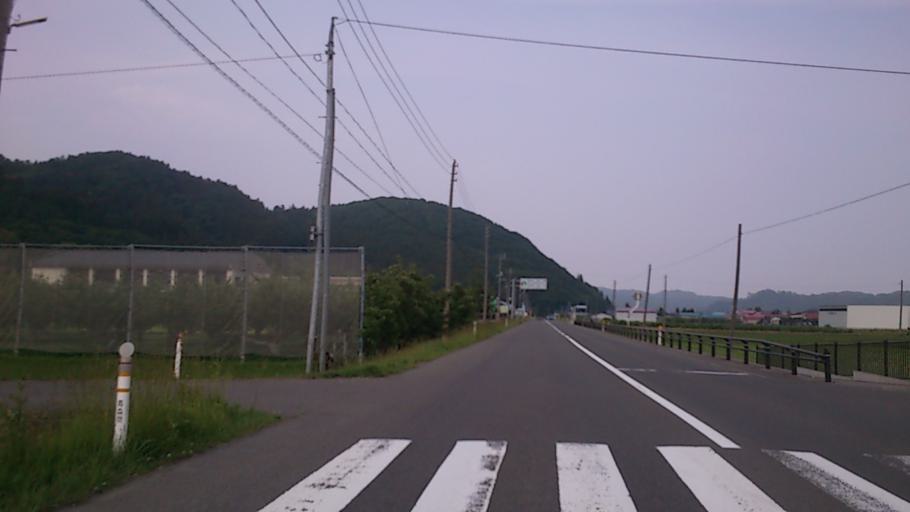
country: JP
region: Aomori
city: Hirosaki
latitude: 40.5883
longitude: 140.3207
